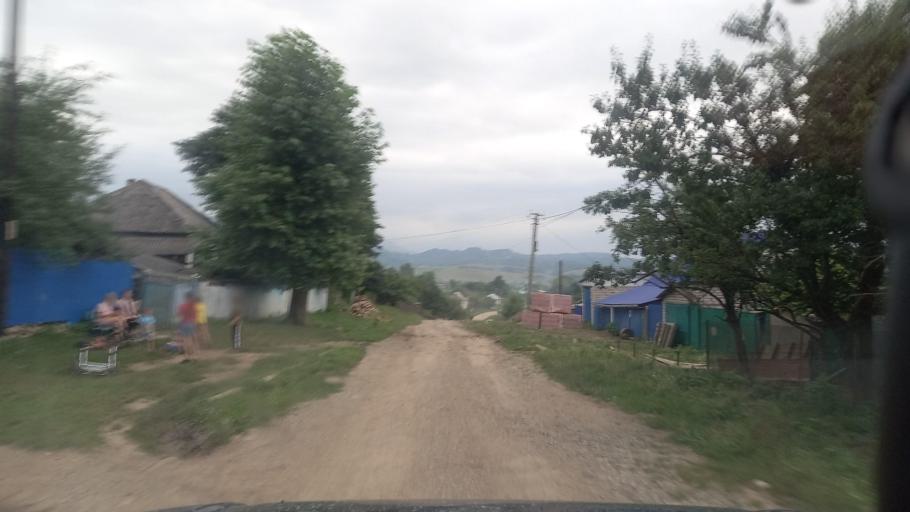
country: RU
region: Karachayevo-Cherkesiya
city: Pregradnaya
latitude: 43.9514
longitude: 41.1774
